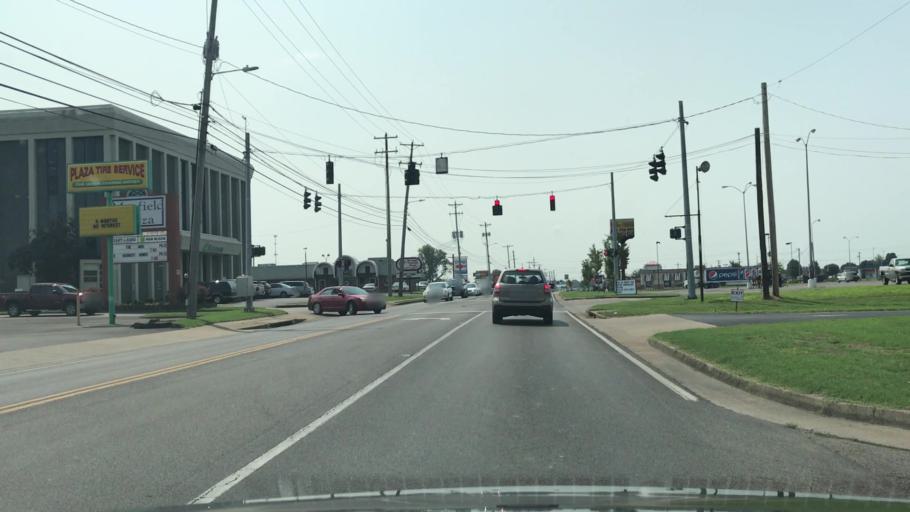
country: US
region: Kentucky
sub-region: Graves County
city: Mayfield
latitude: 36.7254
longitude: -88.6289
